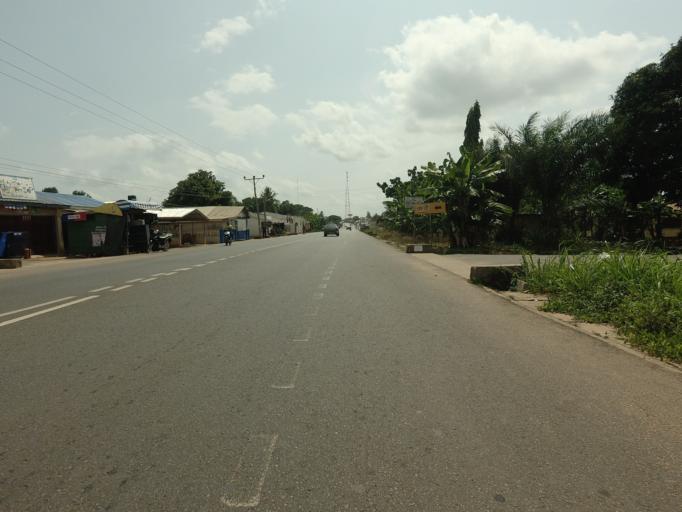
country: TG
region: Maritime
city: Lome
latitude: 6.2309
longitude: 1.0065
